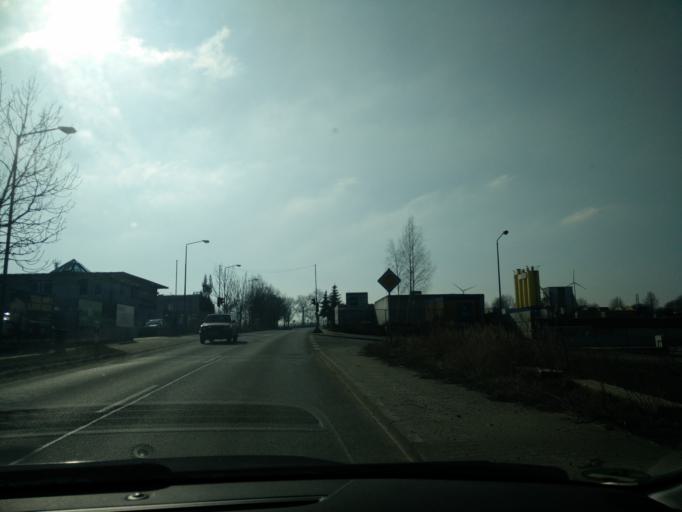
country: DE
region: Saxony
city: Penig
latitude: 50.9492
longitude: 12.6801
